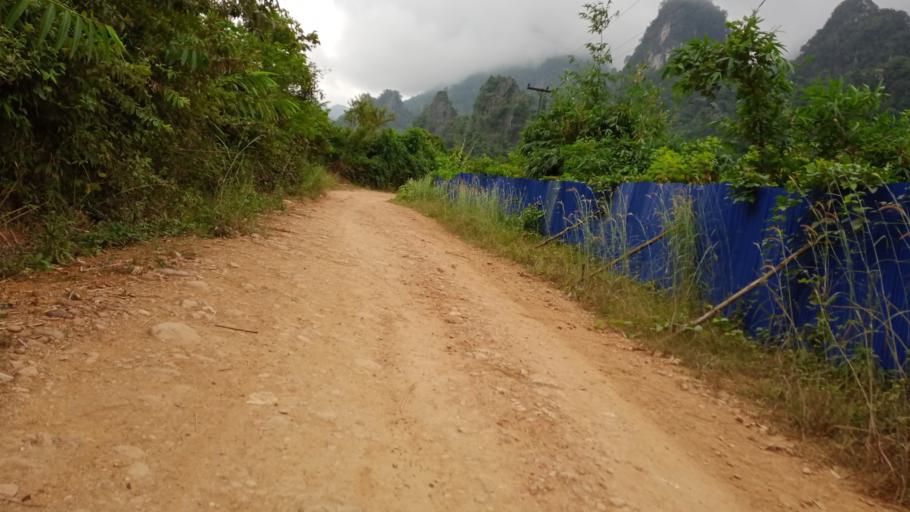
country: LA
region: Xiangkhoang
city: Phonsavan
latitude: 19.0904
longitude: 103.0062
